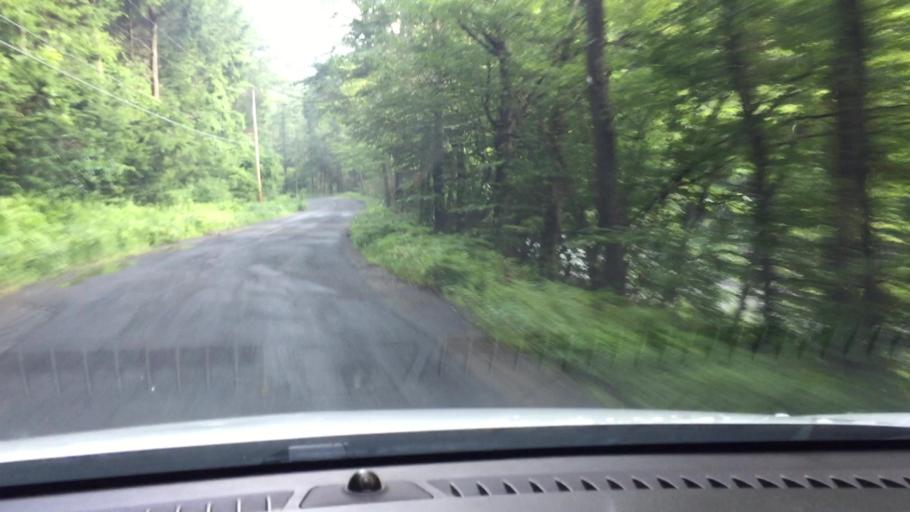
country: US
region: Massachusetts
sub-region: Hampshire County
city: Chesterfield
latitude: 42.3086
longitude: -72.9120
